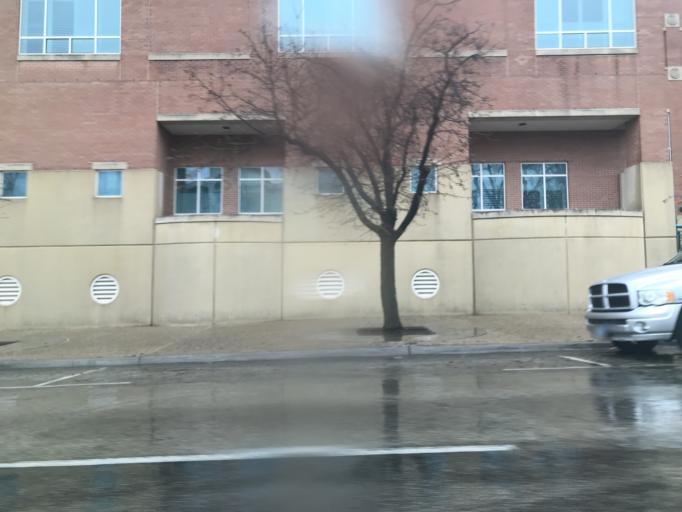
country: US
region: Texas
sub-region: Tom Green County
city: San Angelo
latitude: 31.4652
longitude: -100.4329
